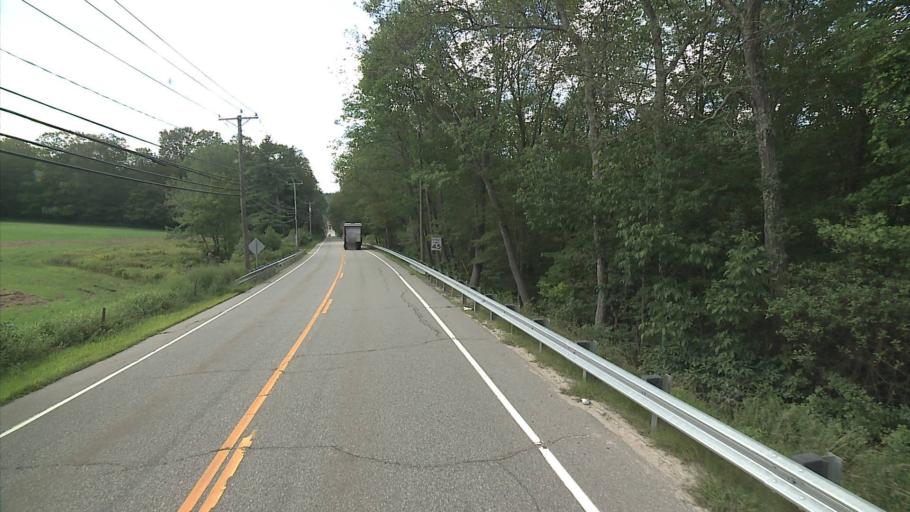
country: US
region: Connecticut
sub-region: Tolland County
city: Stafford
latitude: 41.9631
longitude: -72.2387
